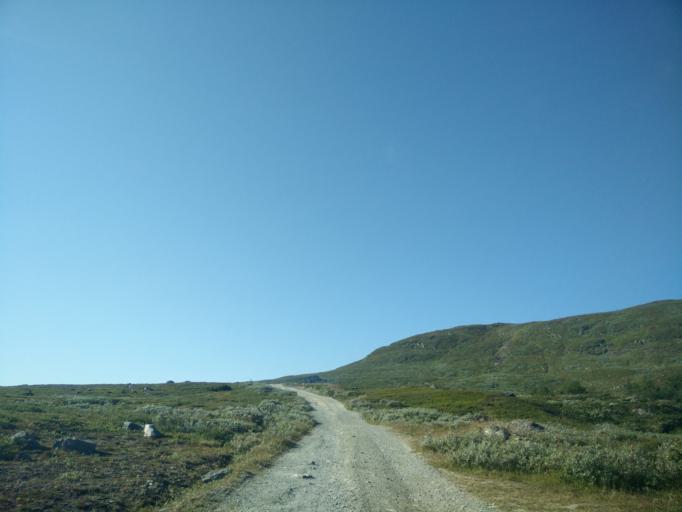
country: NO
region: Sor-Trondelag
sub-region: Tydal
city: Aas
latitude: 62.5711
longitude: 12.1977
